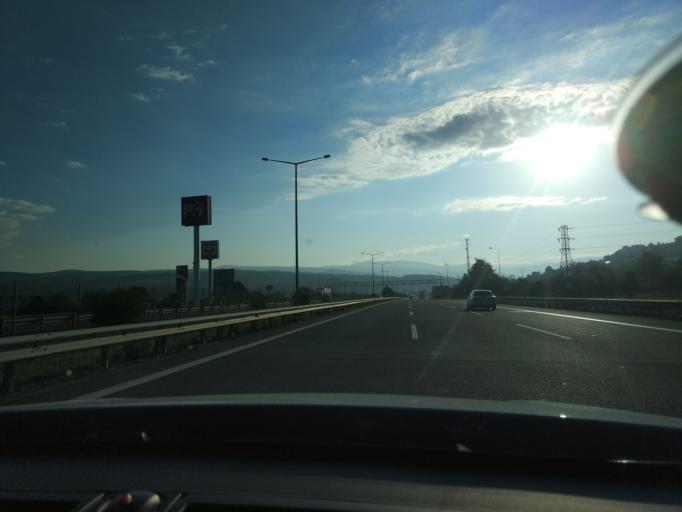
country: TR
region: Duzce
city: Kaynasli
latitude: 40.7904
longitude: 31.2430
